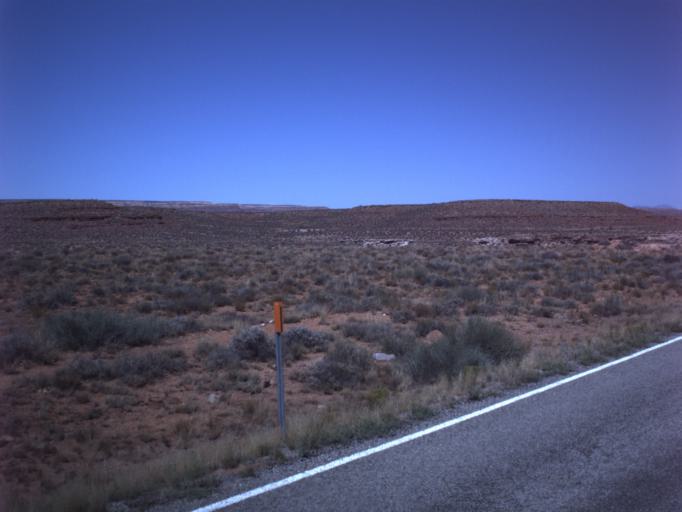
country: US
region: Arizona
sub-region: Navajo County
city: Kayenta
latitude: 37.1896
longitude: -109.9130
